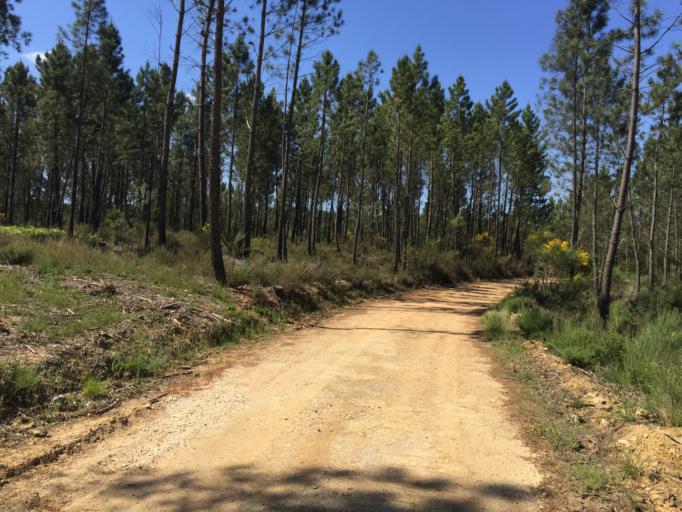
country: PT
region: Coimbra
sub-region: Pampilhosa da Serra
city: Pampilhosa da Serra
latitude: 40.0778
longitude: -7.7787
